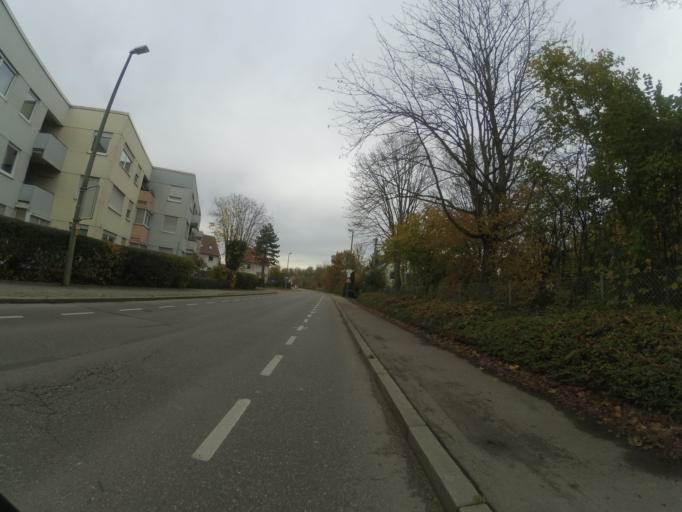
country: DE
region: Baden-Wuerttemberg
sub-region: Tuebingen Region
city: Ulm
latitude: 48.3633
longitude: 9.9900
